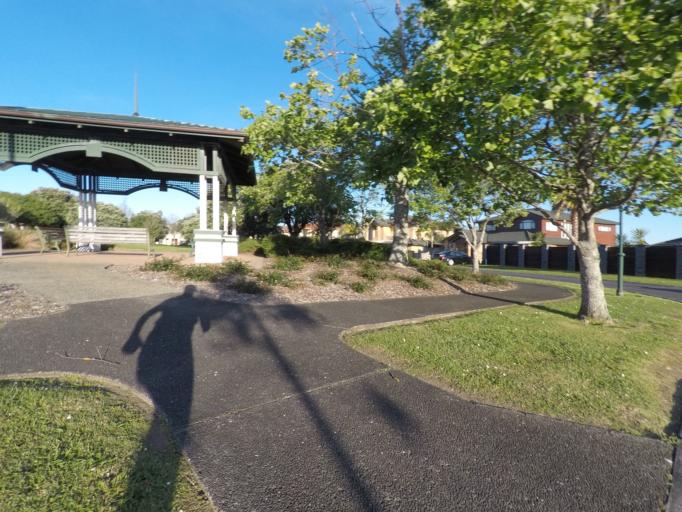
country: NZ
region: Auckland
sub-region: Auckland
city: Rosebank
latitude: -36.8470
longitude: 174.6524
